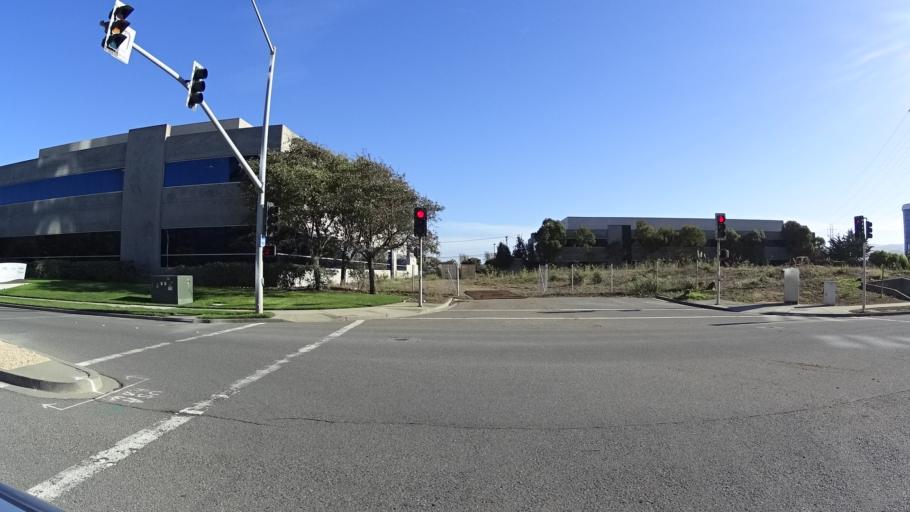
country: US
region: California
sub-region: San Mateo County
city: South San Francisco
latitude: 37.6576
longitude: -122.3995
